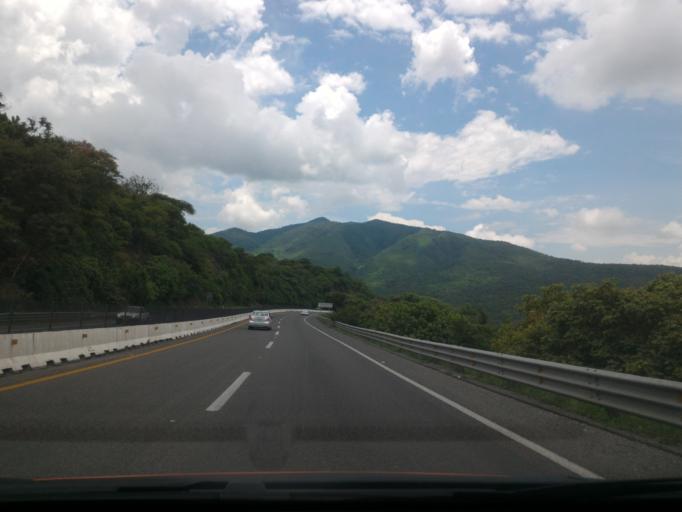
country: MX
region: Jalisco
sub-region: Acatlan de Juarez
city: Villa de los Ninos
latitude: 20.4057
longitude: -103.5588
